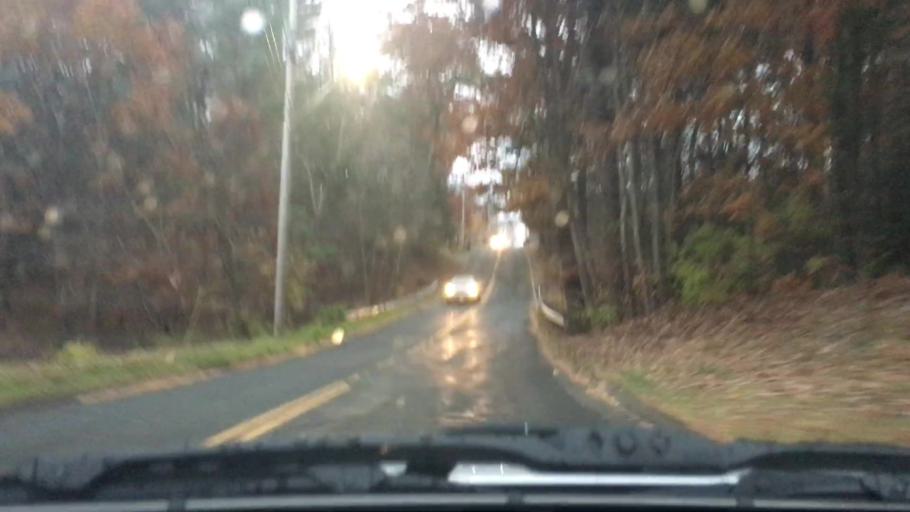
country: US
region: Massachusetts
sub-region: Hampden County
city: Westfield
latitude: 42.1035
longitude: -72.7807
